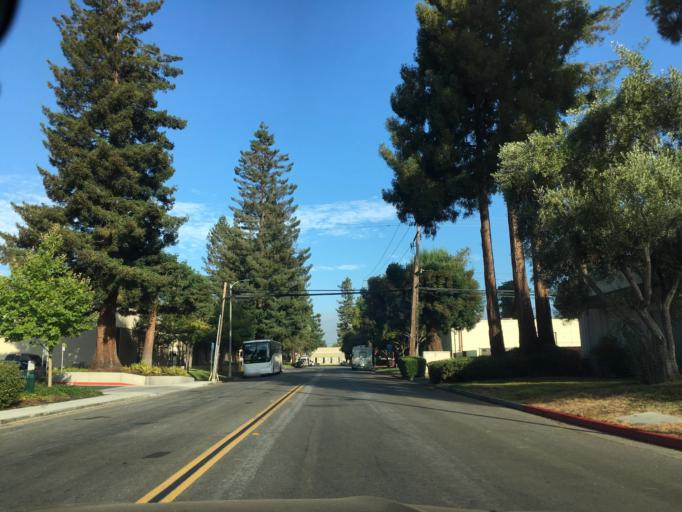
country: US
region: California
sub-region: Santa Clara County
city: Sunnyvale
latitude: 37.3926
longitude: -122.0324
